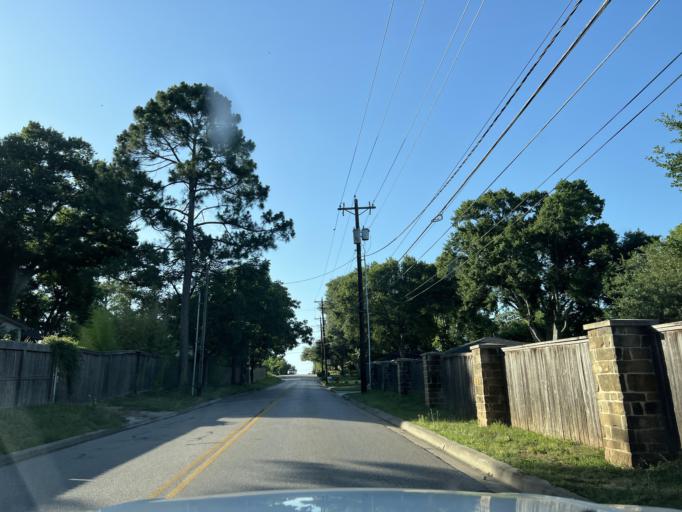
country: US
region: Texas
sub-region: Washington County
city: Brenham
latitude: 30.1557
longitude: -96.3863
